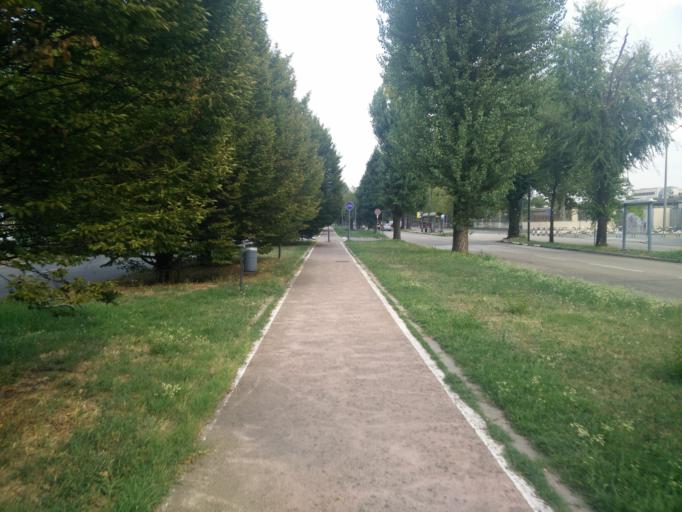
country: IT
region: Piedmont
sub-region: Provincia di Torino
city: Gerbido
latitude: 45.0332
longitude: 7.6319
